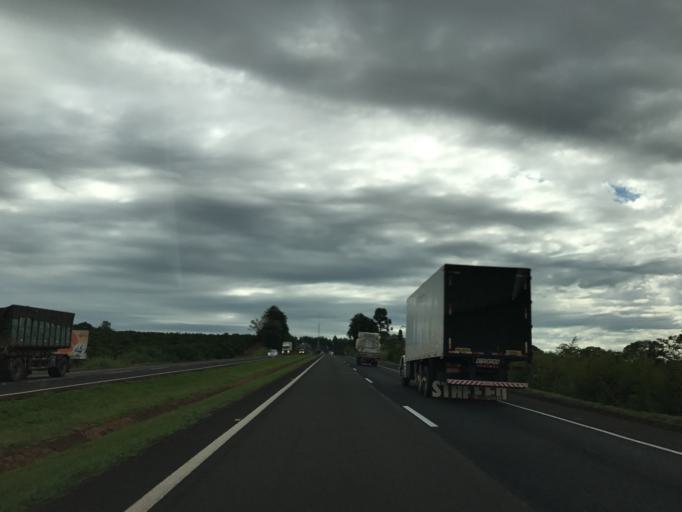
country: BR
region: Parana
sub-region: Rolandia
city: Rolandia
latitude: -23.3092
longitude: -51.3307
